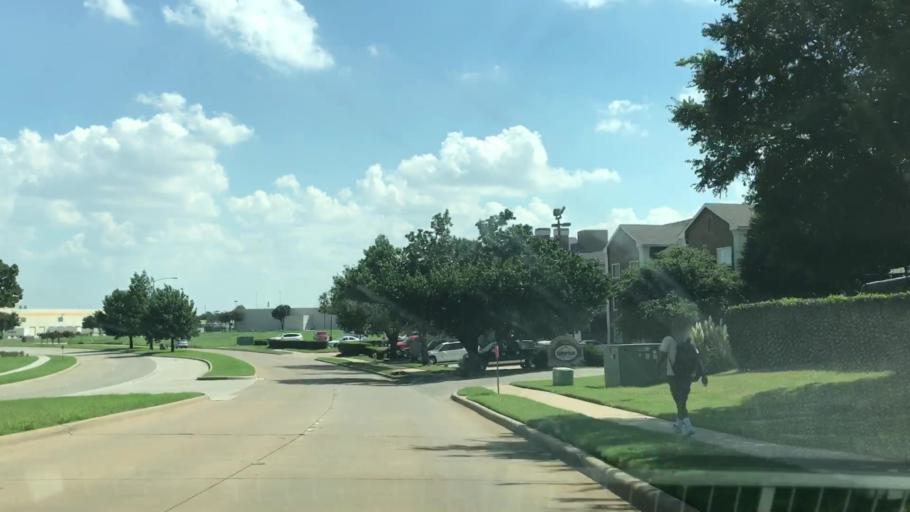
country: US
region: Texas
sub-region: Denton County
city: Lewisville
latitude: 33.0165
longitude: -96.9781
